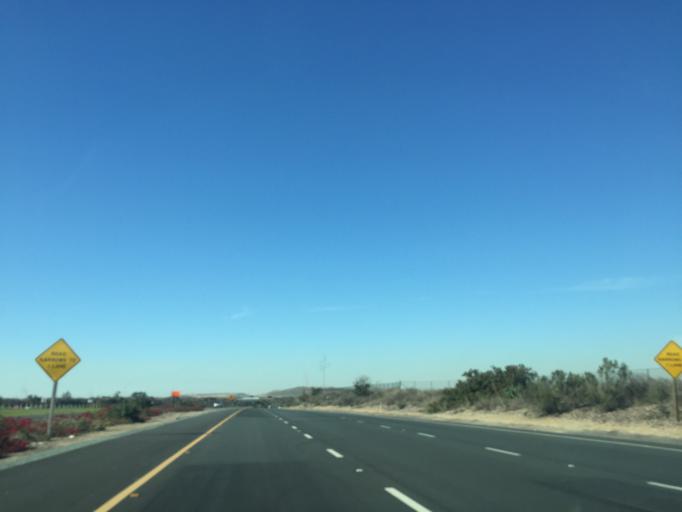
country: MX
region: Baja California
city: Tijuana
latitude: 32.5785
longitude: -116.9591
